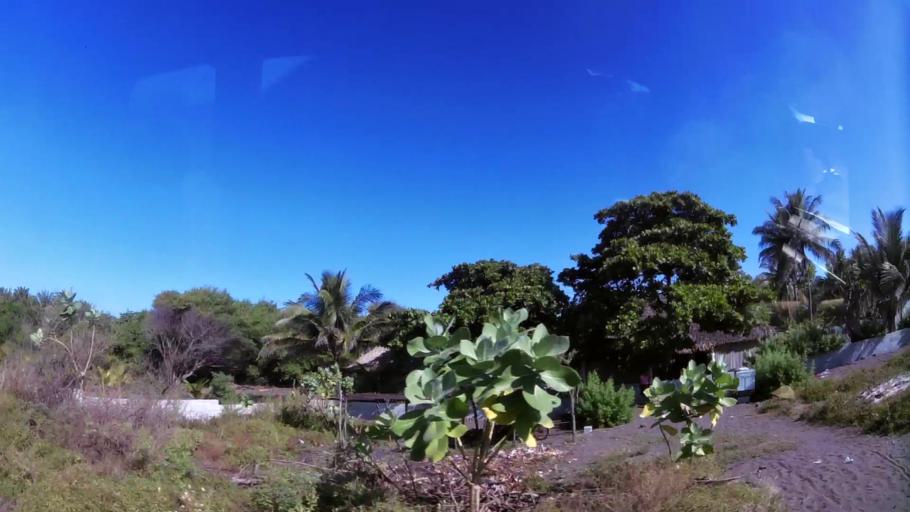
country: GT
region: Jutiapa
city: Pasaco
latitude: 13.8527
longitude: -90.3809
